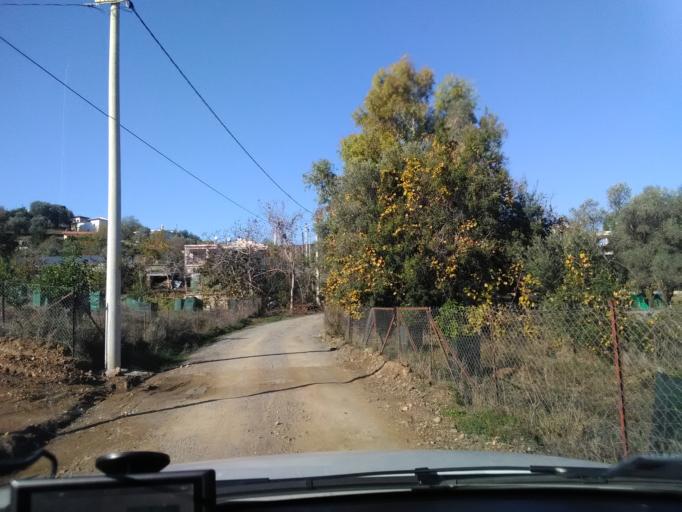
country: TR
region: Antalya
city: Gazipasa
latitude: 36.2468
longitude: 32.3409
